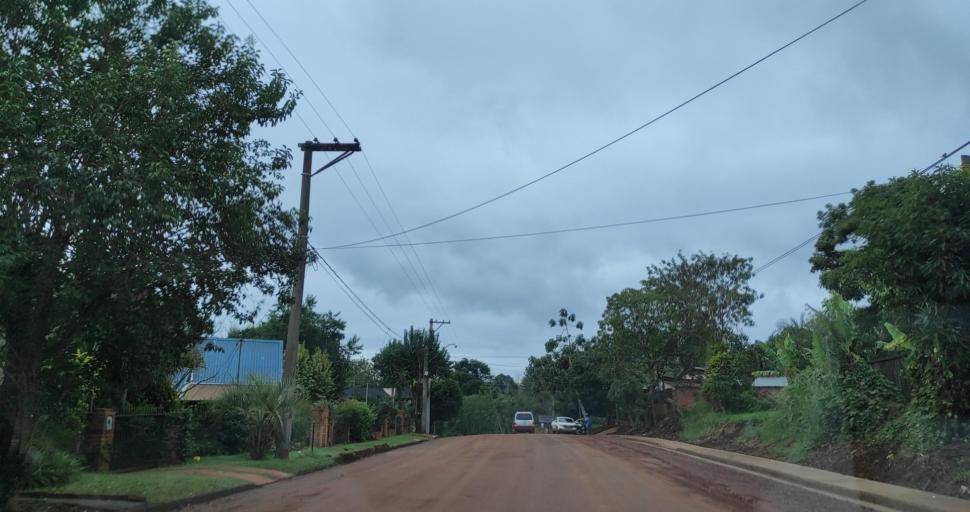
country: AR
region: Misiones
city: Puerto Rico
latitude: -26.7966
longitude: -55.0198
